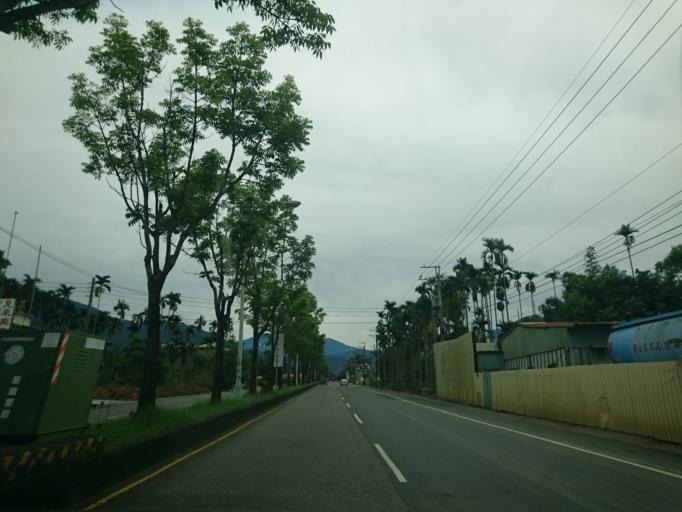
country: TW
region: Taiwan
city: Lugu
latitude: 23.8221
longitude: 120.7779
